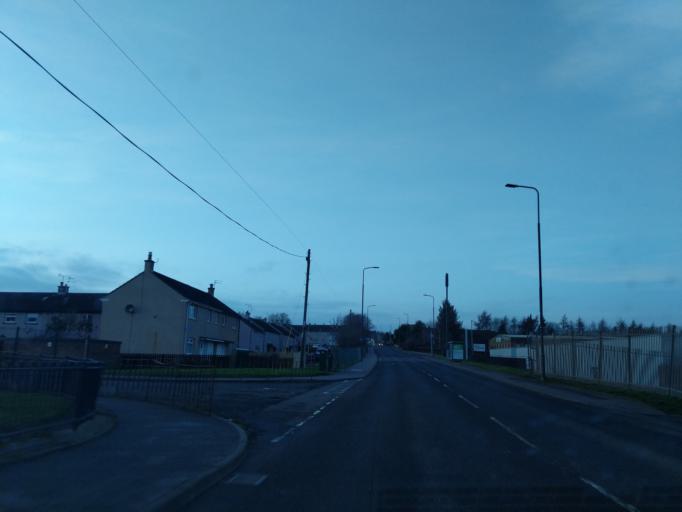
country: GB
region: Scotland
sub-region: Midlothian
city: Bonnyrigg
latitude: 55.8718
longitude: -3.0982
